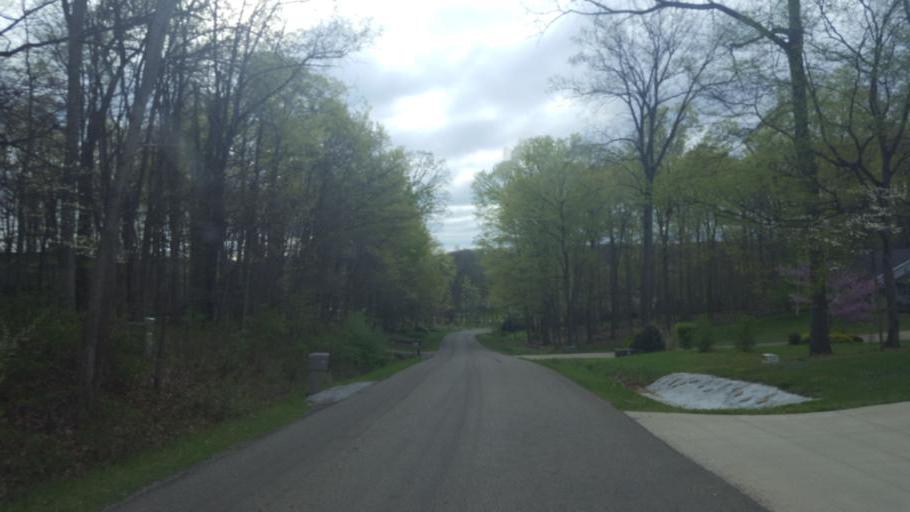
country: US
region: Ohio
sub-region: Knox County
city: Danville
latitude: 40.4599
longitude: -82.3466
